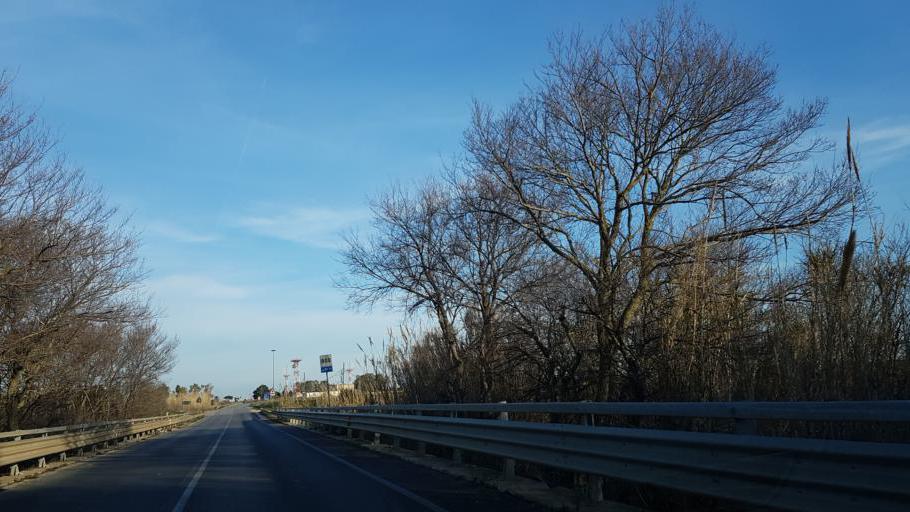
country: IT
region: Apulia
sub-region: Provincia di Brindisi
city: Brindisi
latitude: 40.6487
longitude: 17.8580
